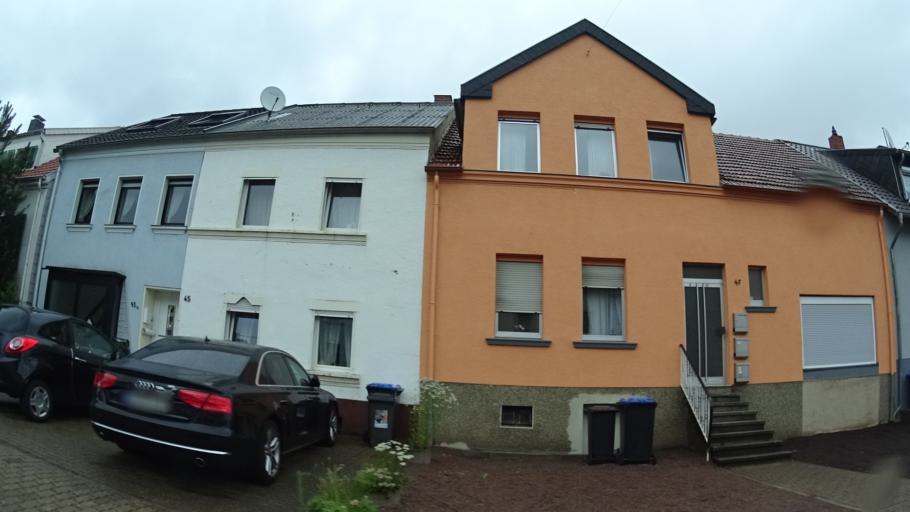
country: DE
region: Saarland
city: Saarwellingen
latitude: 49.3530
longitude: 6.8109
